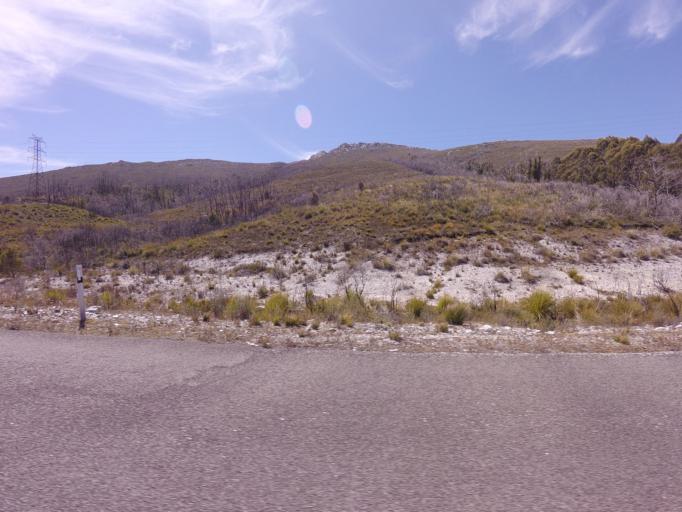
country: AU
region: Tasmania
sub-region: Huon Valley
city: Geeveston
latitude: -42.8439
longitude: 146.1652
